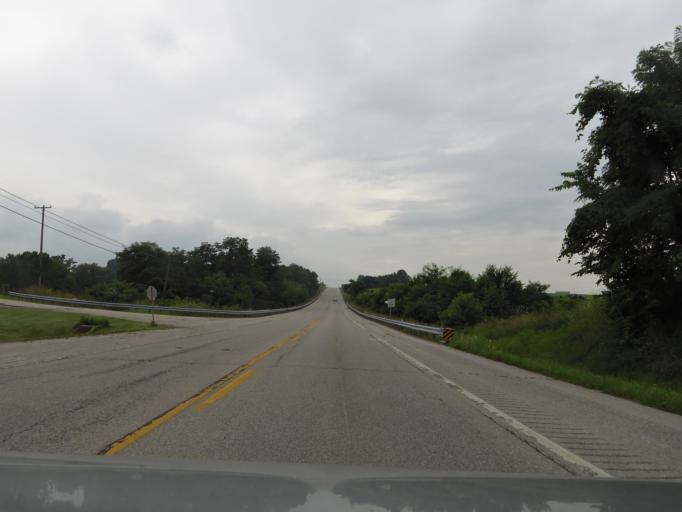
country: US
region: Kentucky
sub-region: Mason County
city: Maysville
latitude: 38.5341
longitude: -83.8296
